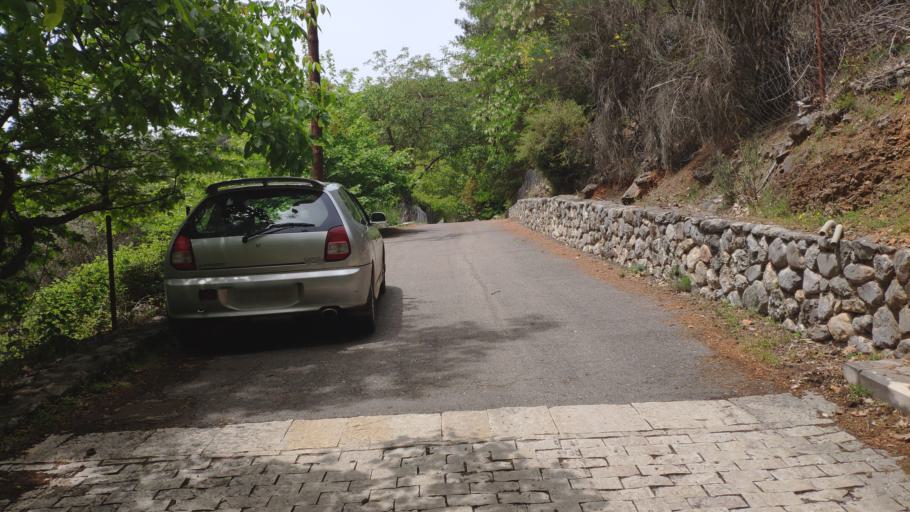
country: GR
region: West Greece
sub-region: Nomos Achaias
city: Kalavryta
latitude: 37.9341
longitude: 22.1658
